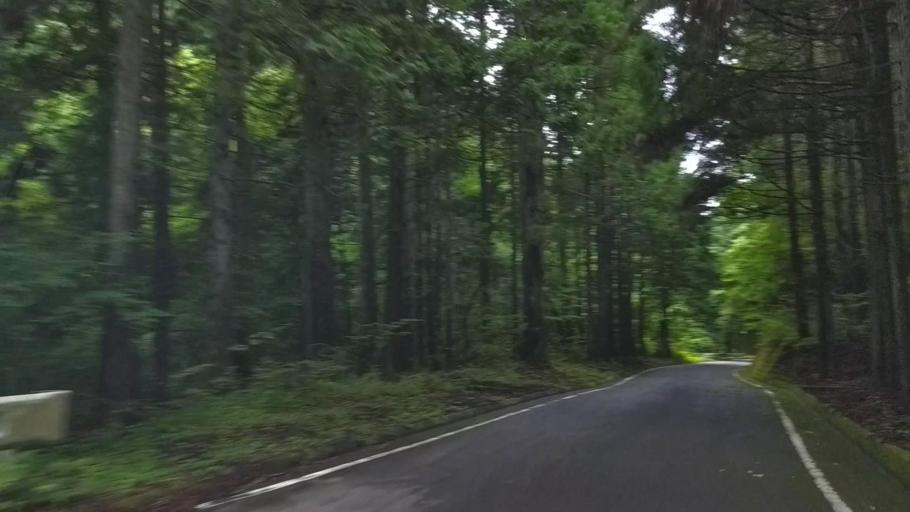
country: JP
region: Shizuoka
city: Gotemba
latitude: 35.3213
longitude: 139.0020
